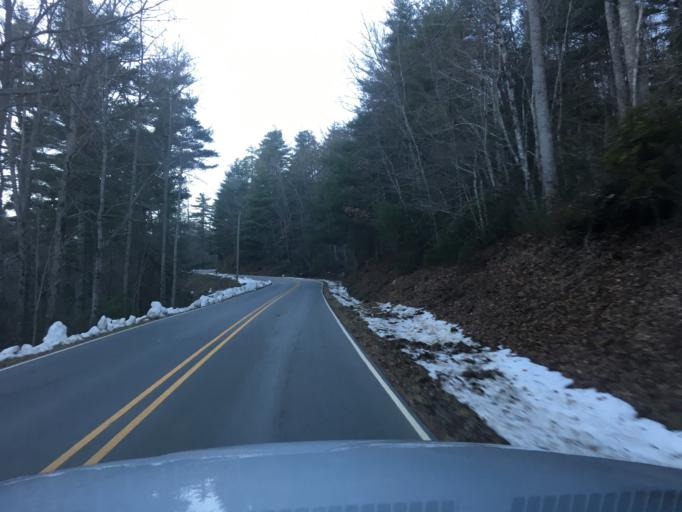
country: US
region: North Carolina
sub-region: Henderson County
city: Flat Rock
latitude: 35.2142
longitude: -82.4818
